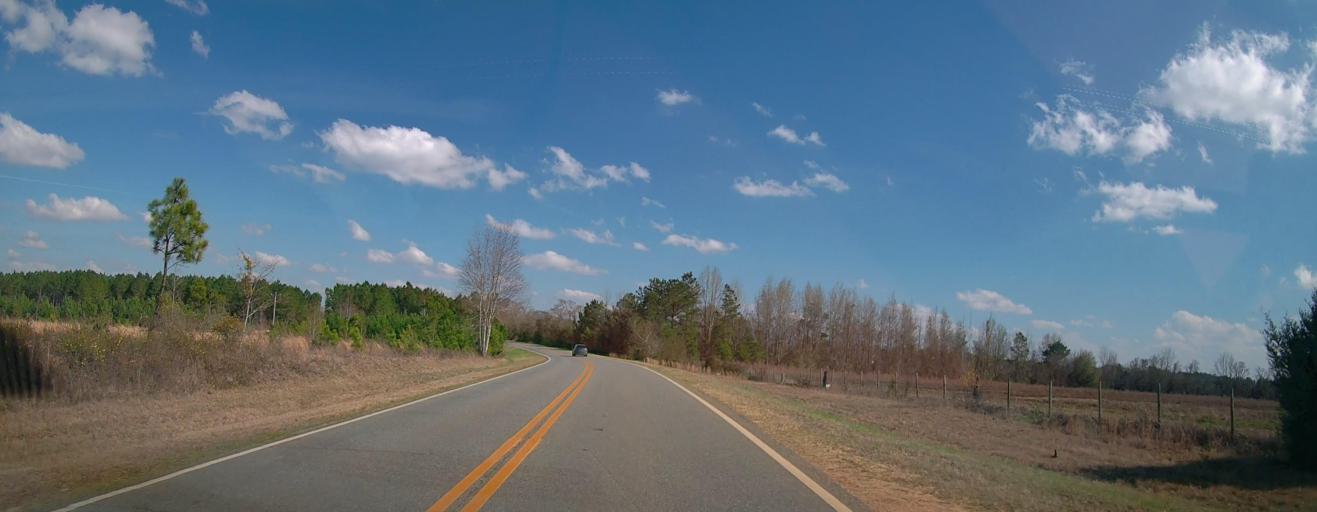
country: US
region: Georgia
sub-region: Laurens County
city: Dublin
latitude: 32.5705
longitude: -83.0408
